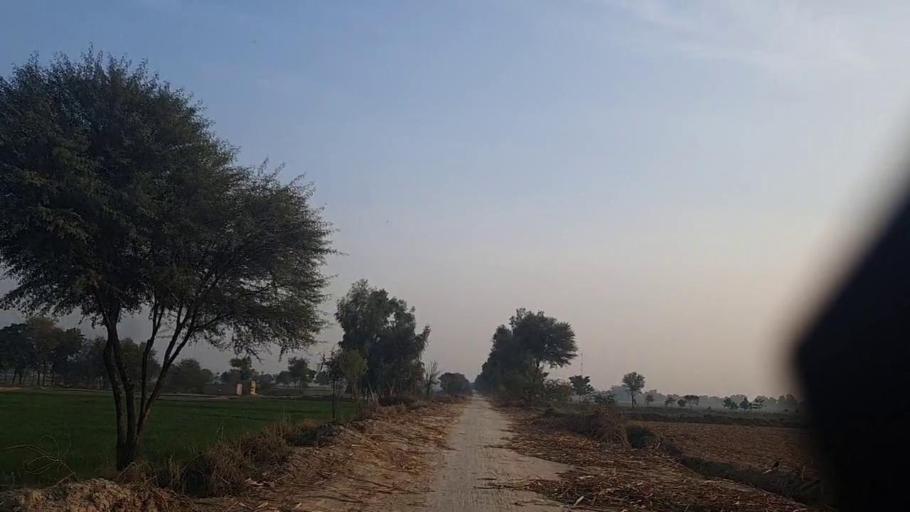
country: PK
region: Sindh
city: Sakrand
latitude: 26.1249
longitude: 68.2302
